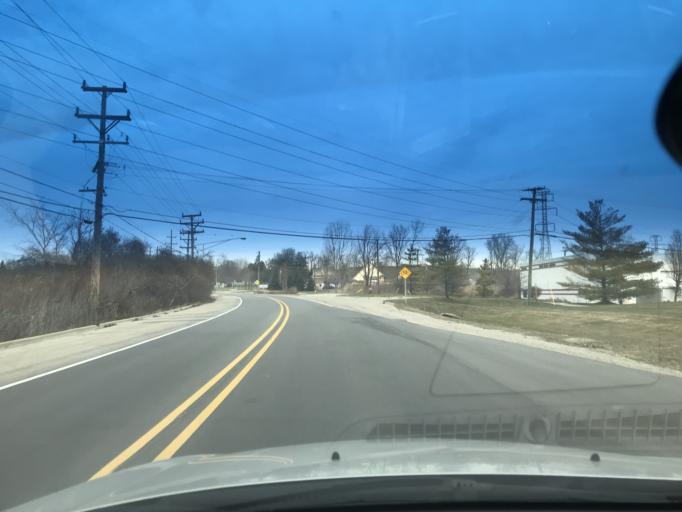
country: US
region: Michigan
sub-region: Macomb County
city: Shelby
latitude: 42.7104
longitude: -83.0549
